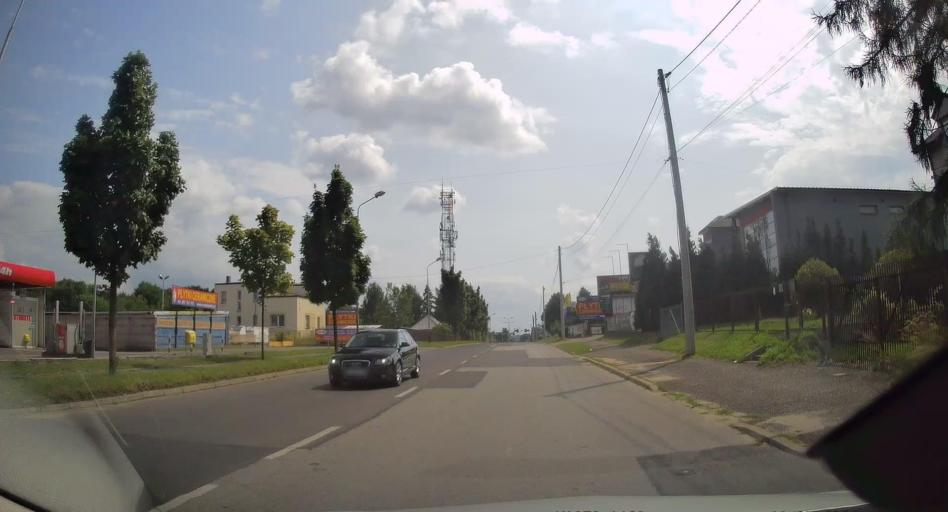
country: PL
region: Silesian Voivodeship
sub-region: Czestochowa
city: Czestochowa
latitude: 50.8162
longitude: 19.0851
